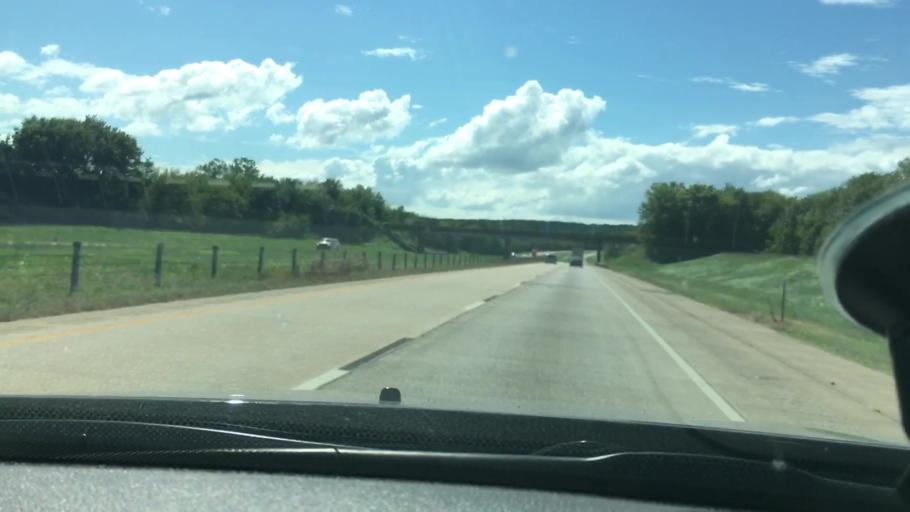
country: US
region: Oklahoma
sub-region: Sequoyah County
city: Vian
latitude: 35.4907
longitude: -95.0235
